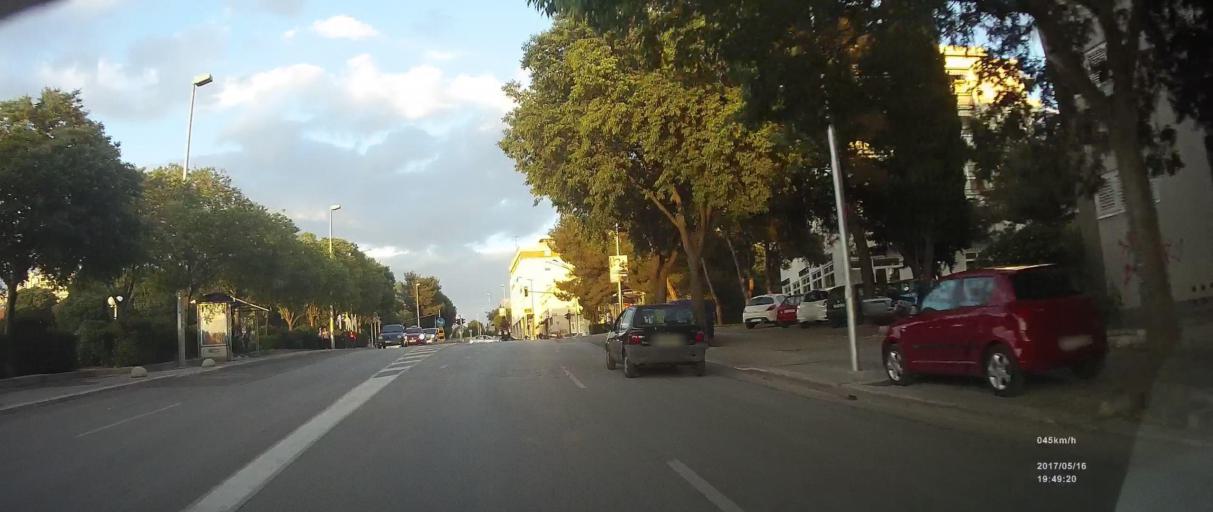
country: HR
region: Splitsko-Dalmatinska
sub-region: Grad Split
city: Split
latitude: 43.5080
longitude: 16.4519
